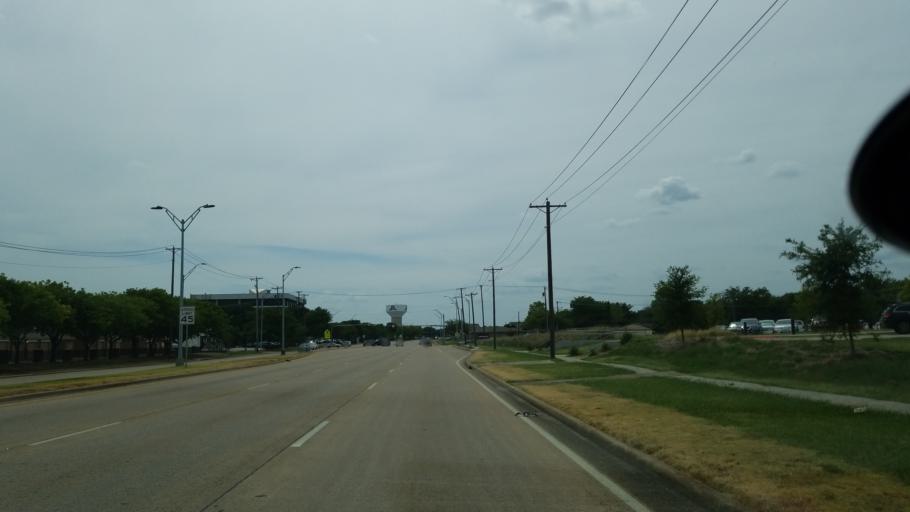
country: US
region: Texas
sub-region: Tarrant County
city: Arlington
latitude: 32.7096
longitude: -97.0833
